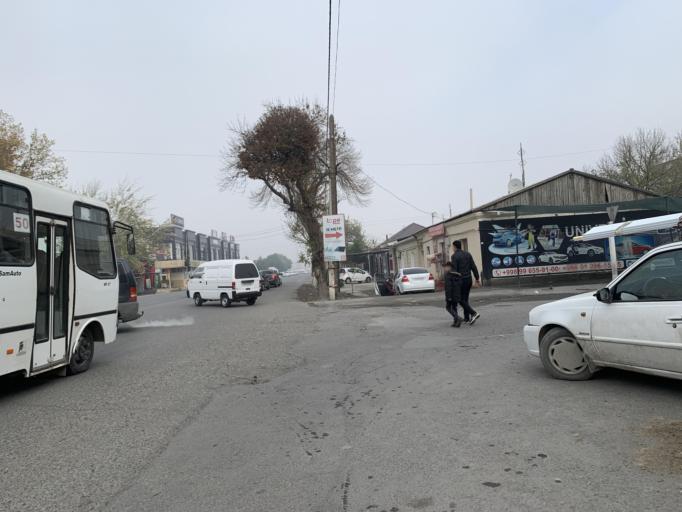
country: UZ
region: Fergana
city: Qo`qon
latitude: 40.5473
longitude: 70.9573
